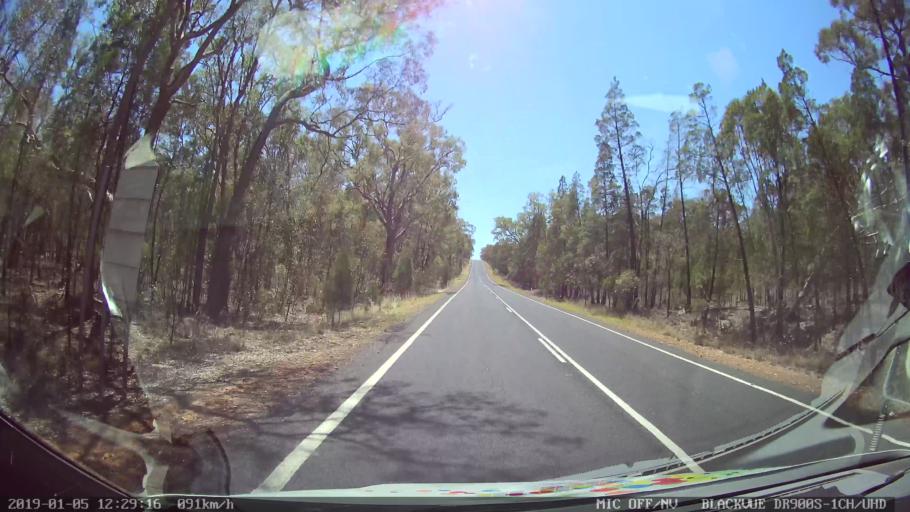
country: AU
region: New South Wales
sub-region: Warrumbungle Shire
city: Coonabarabran
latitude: -31.2344
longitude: 149.3348
